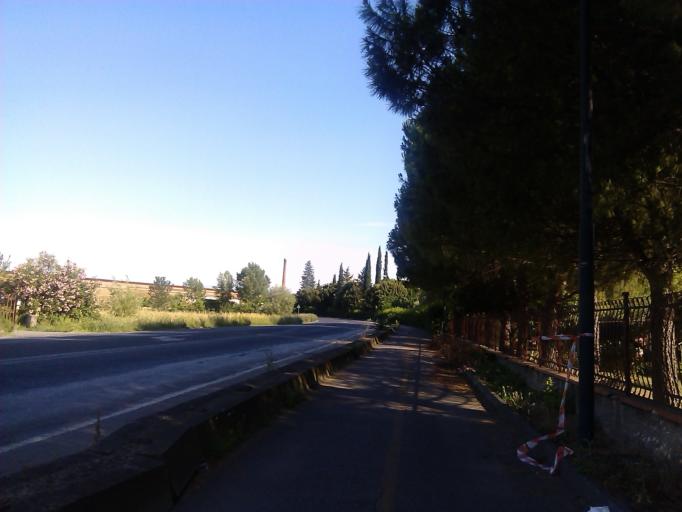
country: IT
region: Tuscany
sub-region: Province of Florence
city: Campi Bisenzio
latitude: 43.8199
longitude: 11.1486
